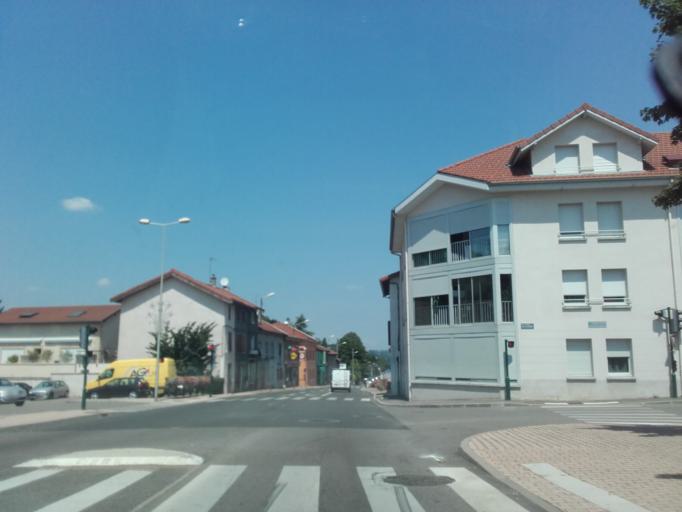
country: FR
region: Rhone-Alpes
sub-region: Departement de l'Isere
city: Nivolas-Vermelle
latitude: 45.5566
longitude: 5.3051
